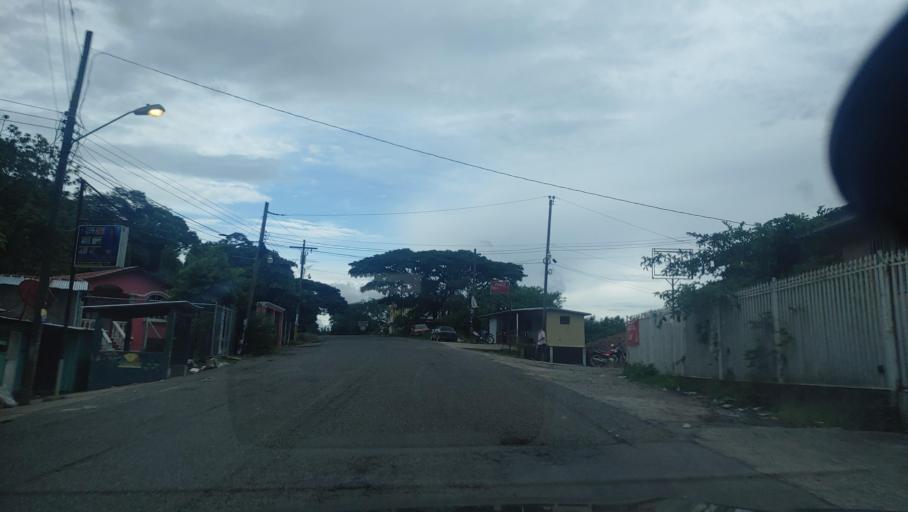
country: HN
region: Choluteca
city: Corpus
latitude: 13.3608
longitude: -86.9890
